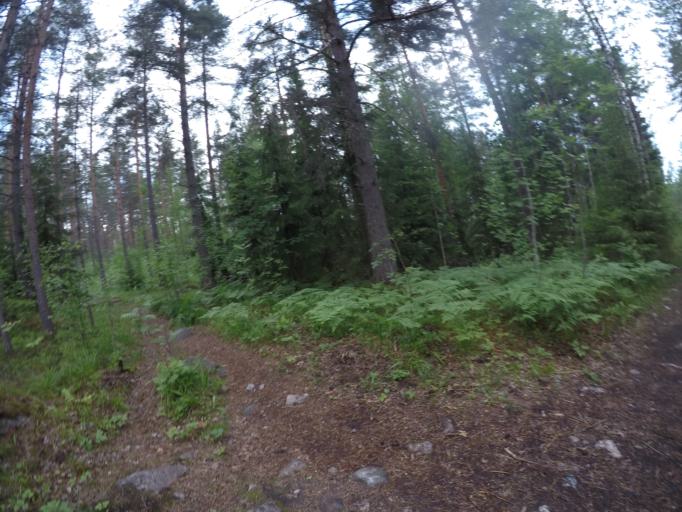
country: FI
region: Haeme
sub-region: Haemeenlinna
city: Haemeenlinna
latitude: 61.0147
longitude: 24.4902
